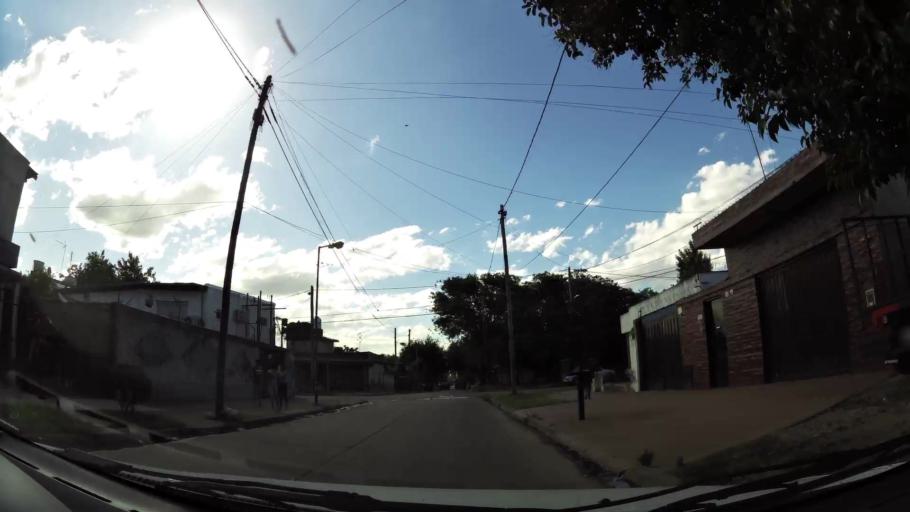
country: AR
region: Buenos Aires
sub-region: Partido de General San Martin
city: General San Martin
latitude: -34.5260
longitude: -58.5808
